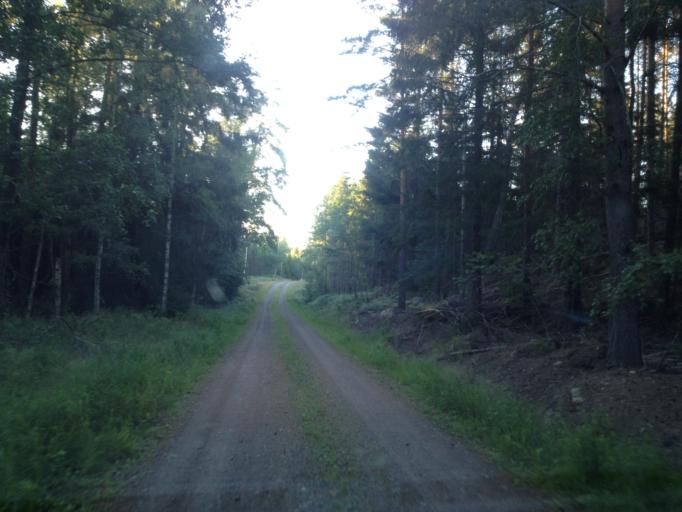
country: SE
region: Kalmar
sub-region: Vasterviks Kommun
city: Overum
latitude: 57.9941
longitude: 16.1695
